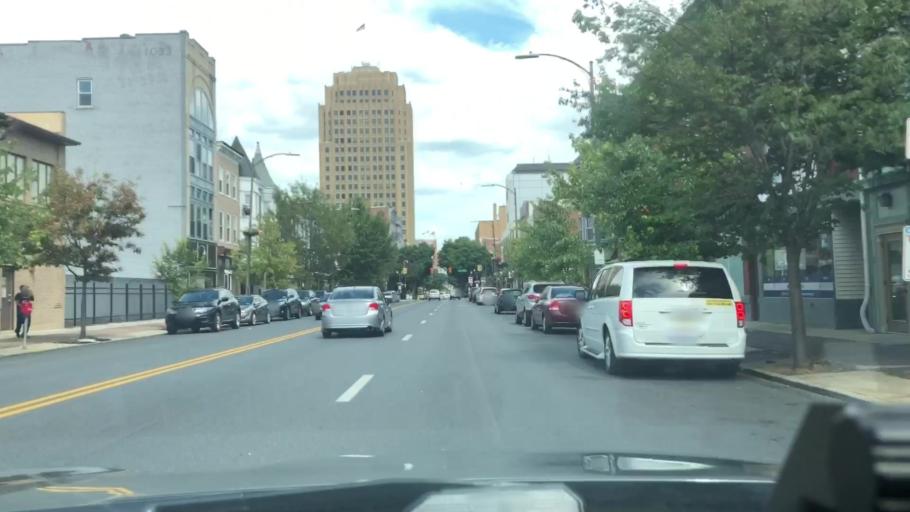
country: US
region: Pennsylvania
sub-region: Lehigh County
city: Allentown
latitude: 40.6000
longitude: -75.4797
